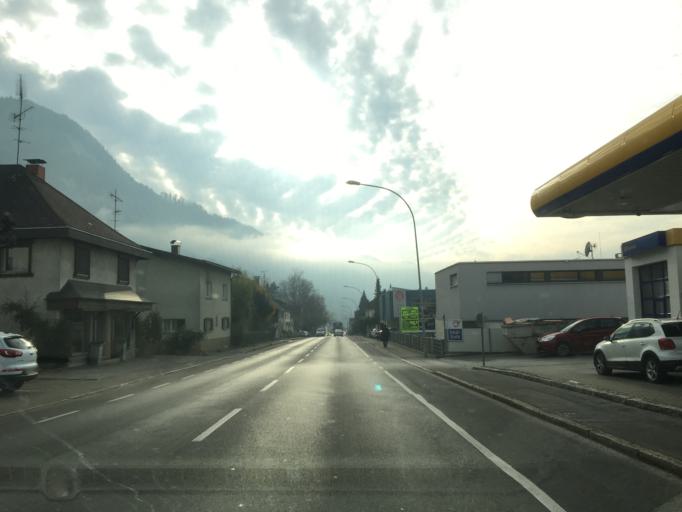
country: AT
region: Vorarlberg
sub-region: Politischer Bezirk Dornbirn
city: Hohenems
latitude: 47.3574
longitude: 9.6834
